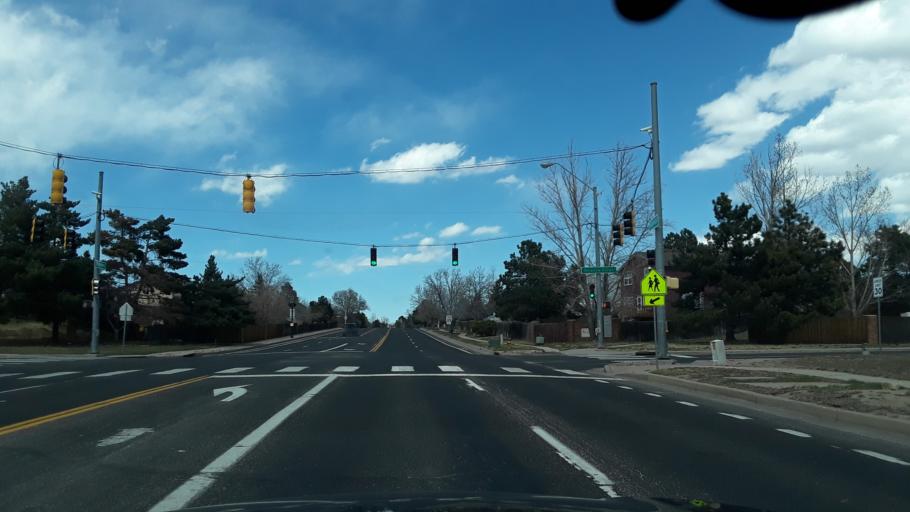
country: US
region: Colorado
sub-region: El Paso County
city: Black Forest
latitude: 38.9470
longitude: -104.7532
